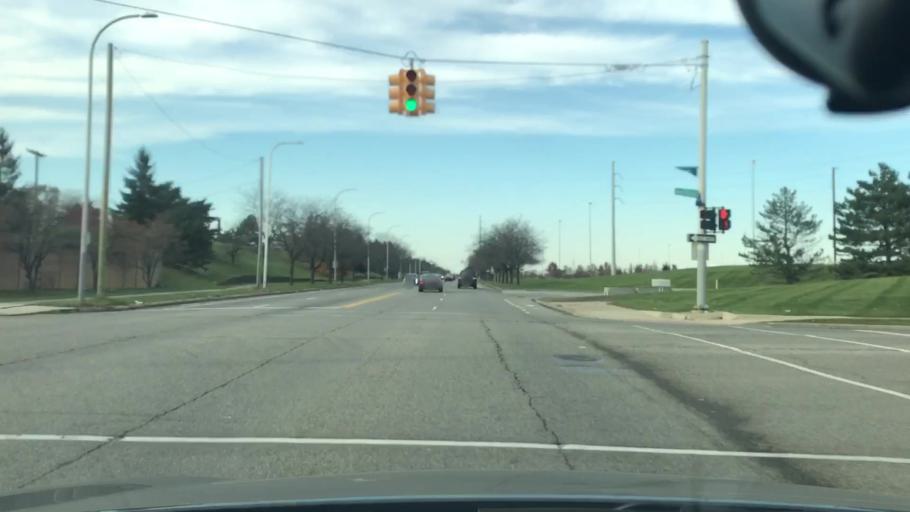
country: US
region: Michigan
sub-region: Wayne County
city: Grosse Pointe Park
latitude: 42.3693
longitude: -82.9720
